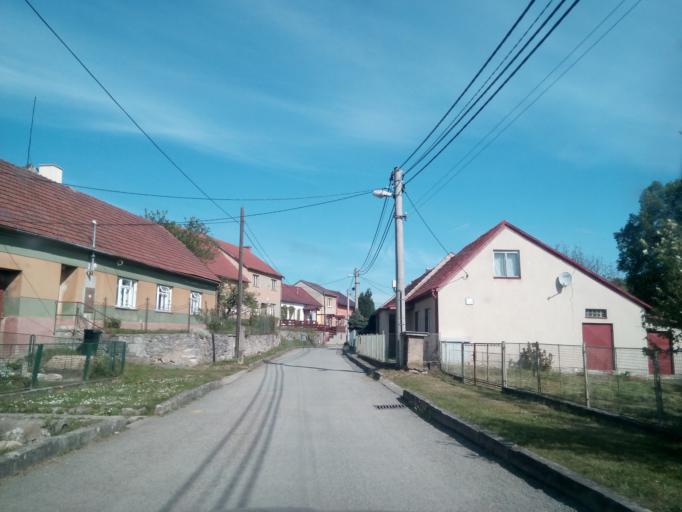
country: CZ
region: South Moravian
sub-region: Okres Blansko
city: Jedovnice
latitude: 49.3641
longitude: 16.7459
